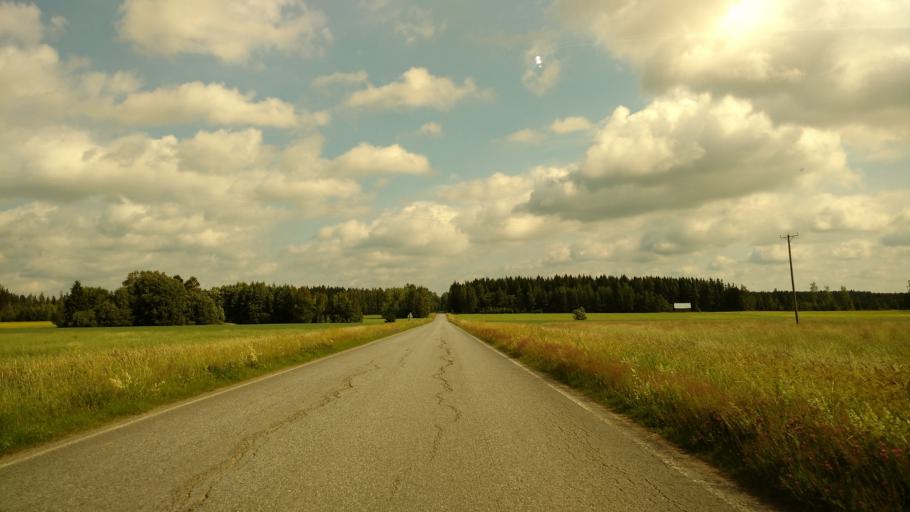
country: FI
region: Haeme
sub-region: Forssa
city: Ypaejae
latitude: 60.7538
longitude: 23.2072
